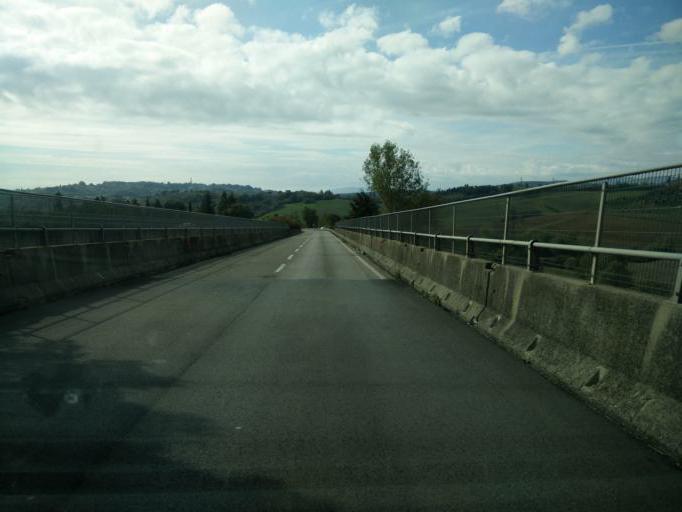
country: IT
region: Tuscany
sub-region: Provincia di Siena
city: Belverde
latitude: 43.3374
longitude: 11.2928
